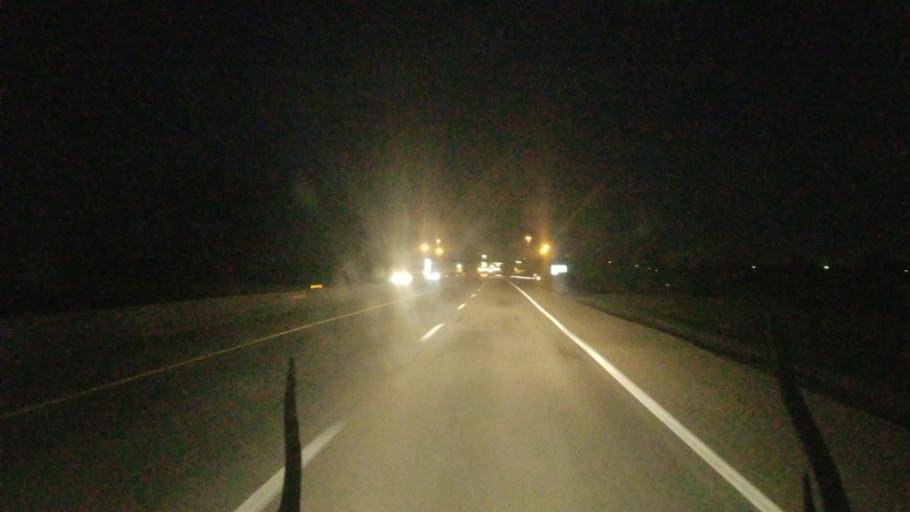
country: US
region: Kansas
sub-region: Douglas County
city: Eudora
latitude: 39.0138
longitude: -95.1457
